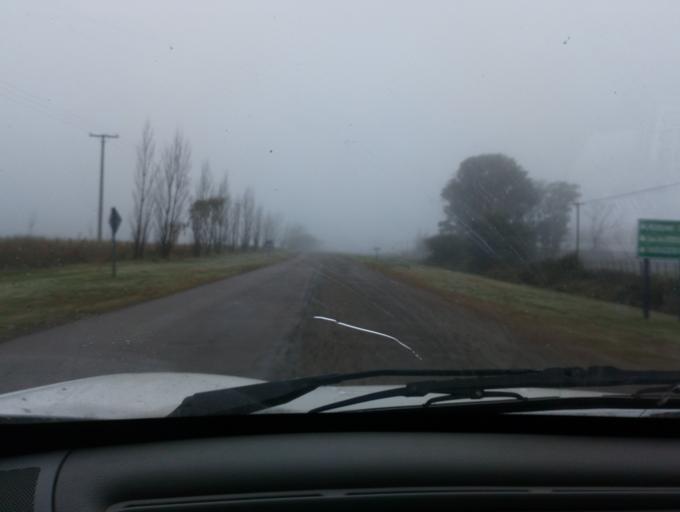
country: AR
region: La Pampa
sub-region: Departamento de Guatrache
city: Guatrache
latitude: -37.6651
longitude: -63.5202
